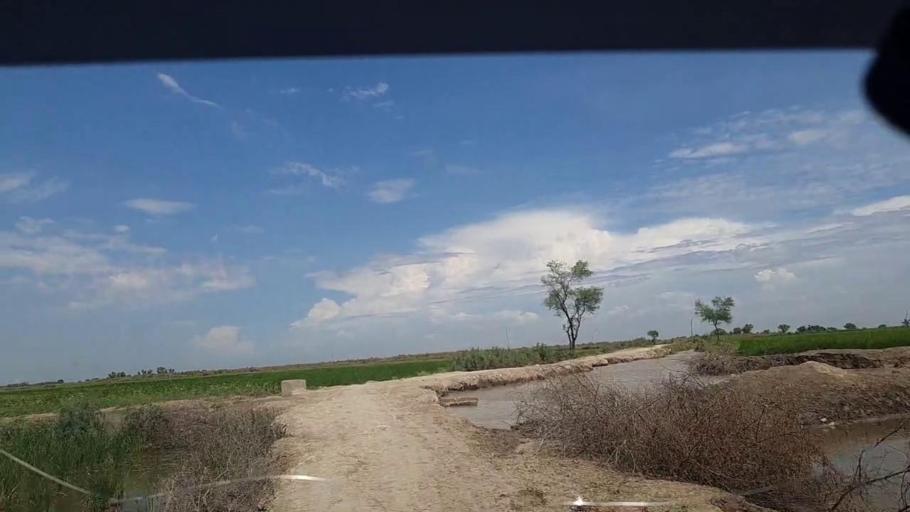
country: PK
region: Sindh
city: Ghauspur
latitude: 28.1488
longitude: 68.9681
